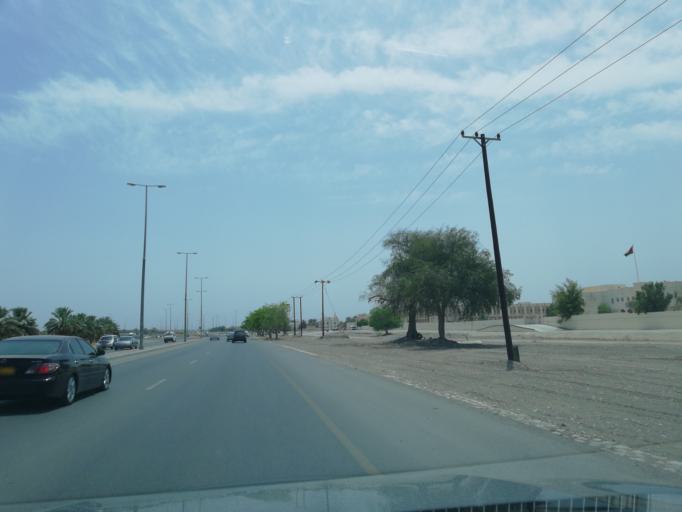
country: OM
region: Muhafazat Masqat
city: As Sib al Jadidah
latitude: 23.6725
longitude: 58.1637
